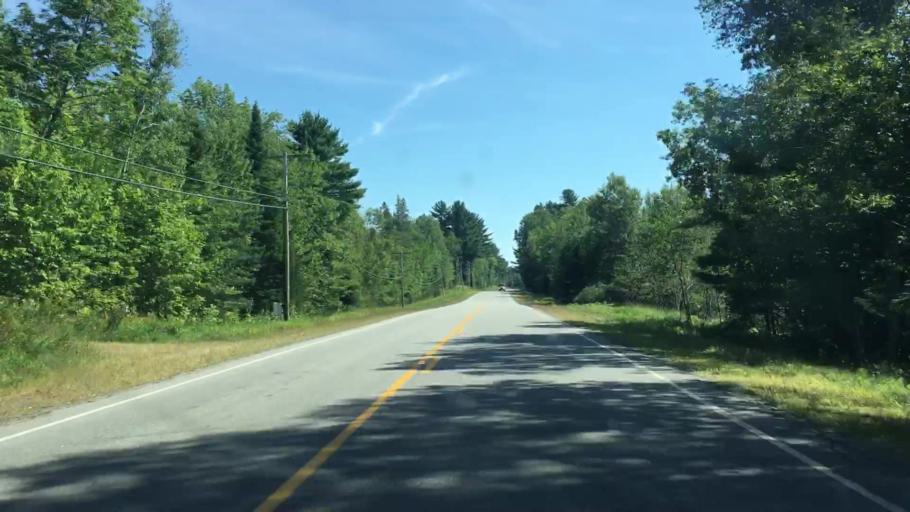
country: US
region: Maine
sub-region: Piscataquis County
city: Milo
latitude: 45.1943
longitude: -68.9014
